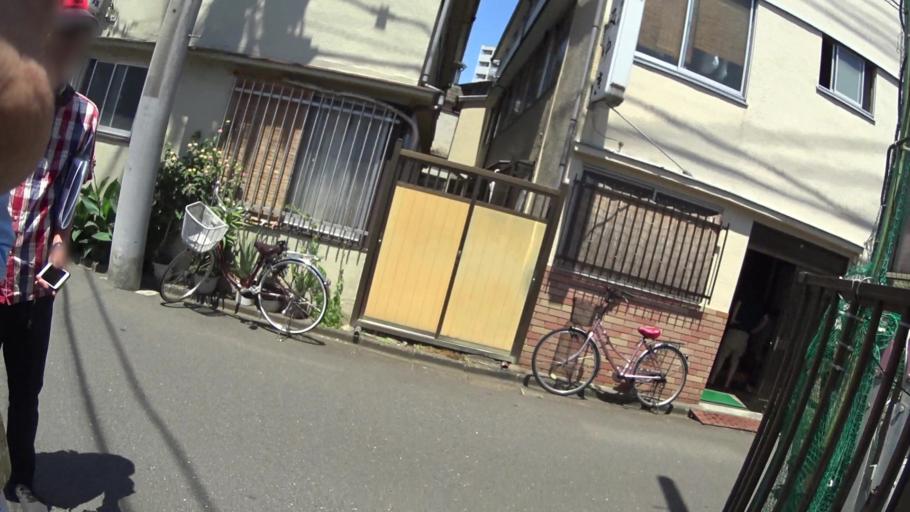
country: JP
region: Kanagawa
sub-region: Kawasaki-shi
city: Kawasaki
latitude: 35.5248
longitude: 139.6924
